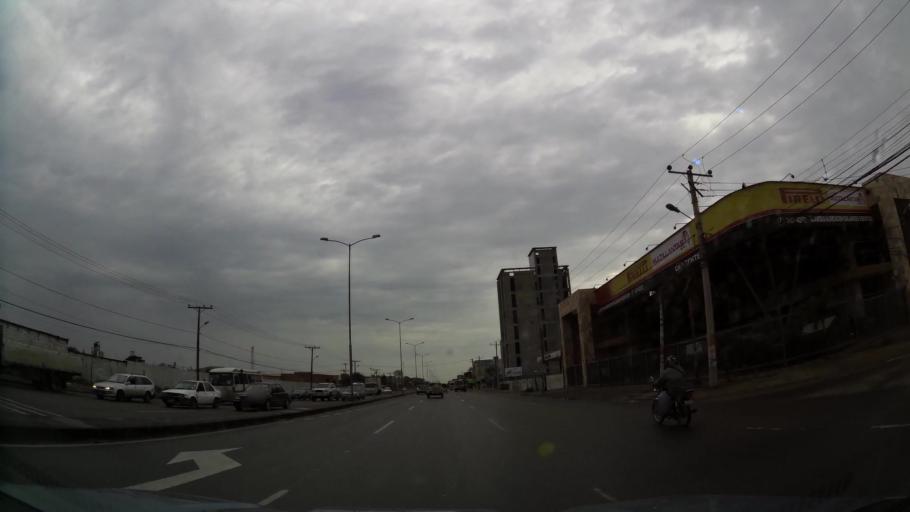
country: BO
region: Santa Cruz
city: Santa Cruz de la Sierra
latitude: -17.7789
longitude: -63.1449
